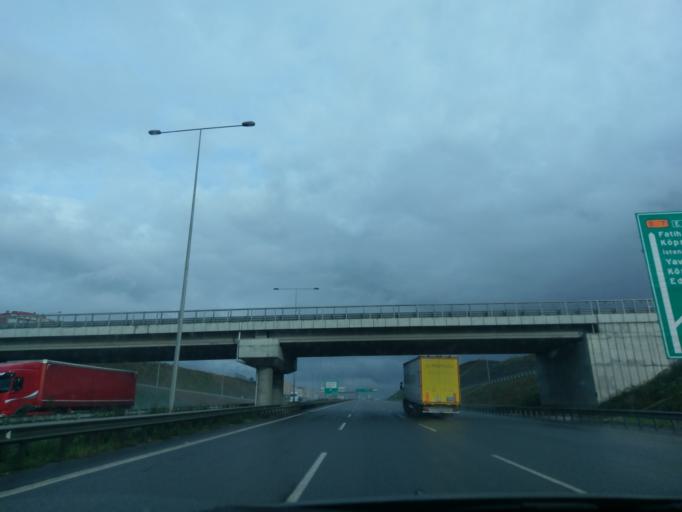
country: TR
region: Istanbul
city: Basaksehir
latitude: 41.0920
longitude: 28.8137
